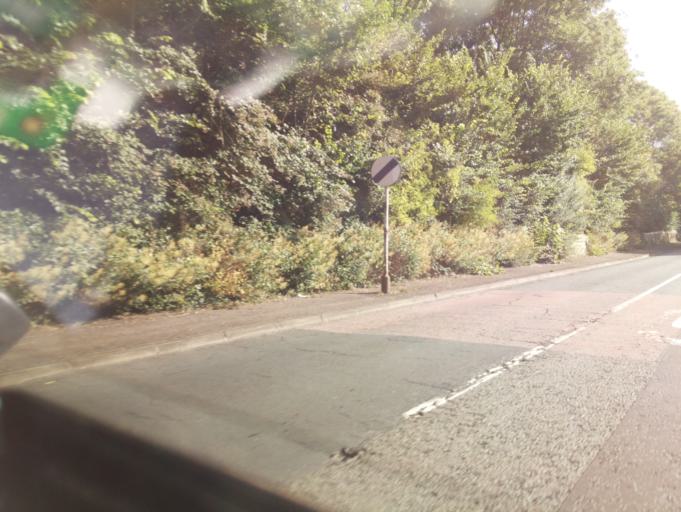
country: GB
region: England
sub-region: Oxfordshire
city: Faringdon
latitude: 51.6591
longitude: -1.5767
